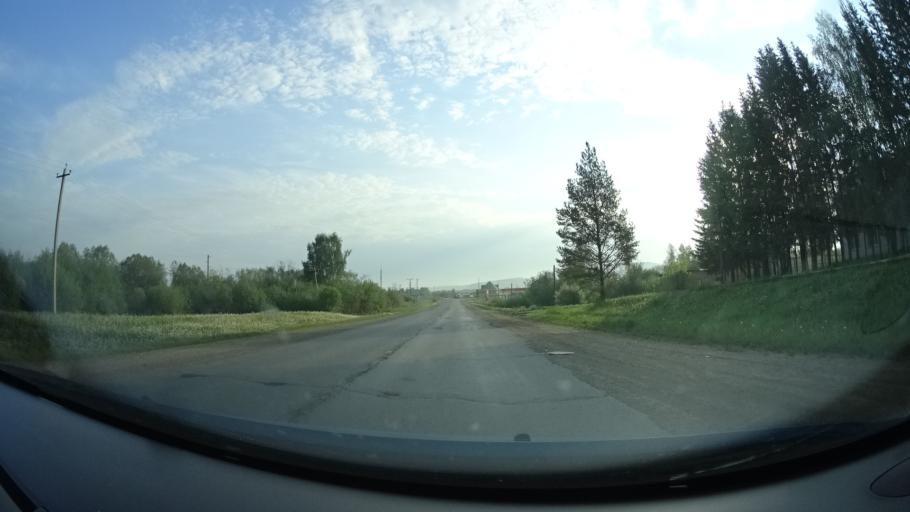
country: RU
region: Perm
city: Barda
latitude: 56.9423
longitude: 55.5893
